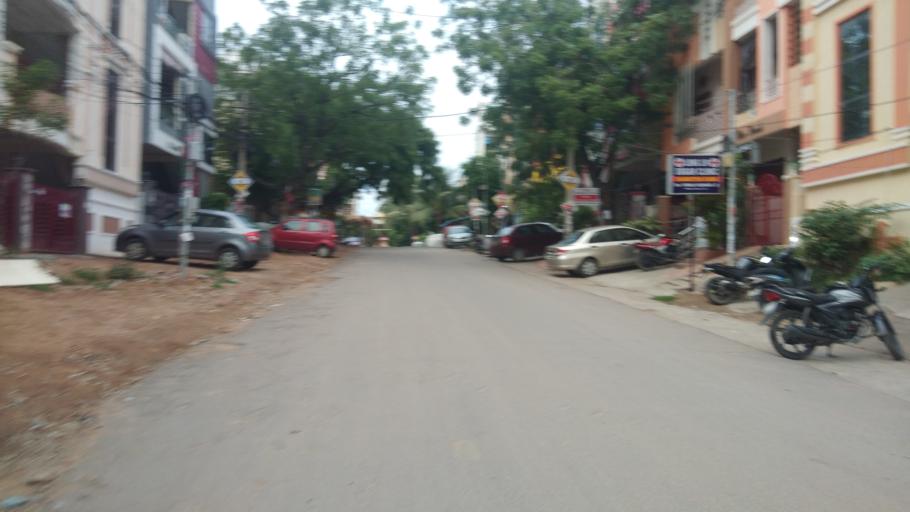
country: IN
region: Telangana
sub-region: Medak
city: Serilingampalle
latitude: 17.4904
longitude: 78.3513
